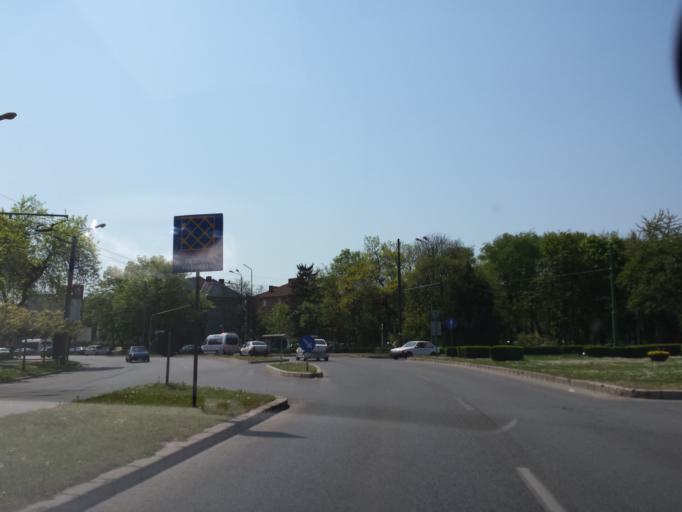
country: RO
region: Timis
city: Timisoara
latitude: 45.7535
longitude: 21.2325
